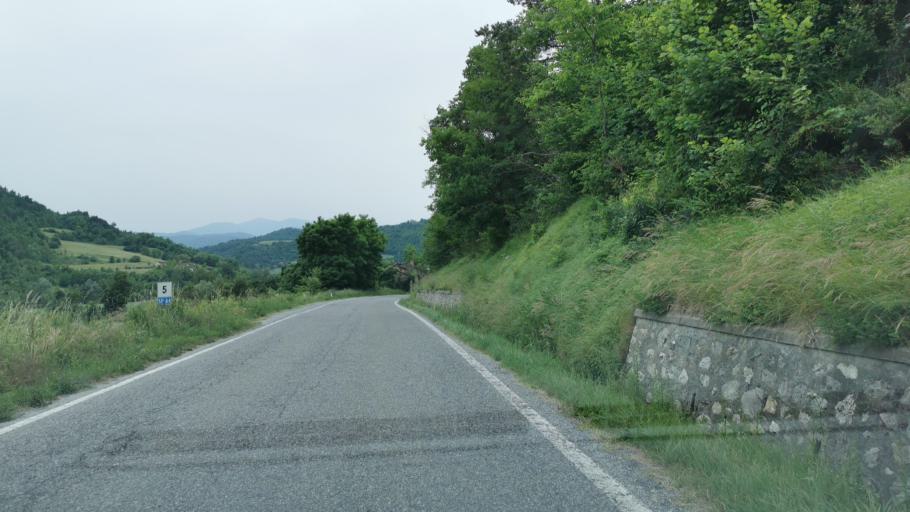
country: IT
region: Piedmont
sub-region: Provincia di Cuneo
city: Paroldo
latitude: 44.4234
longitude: 8.0546
